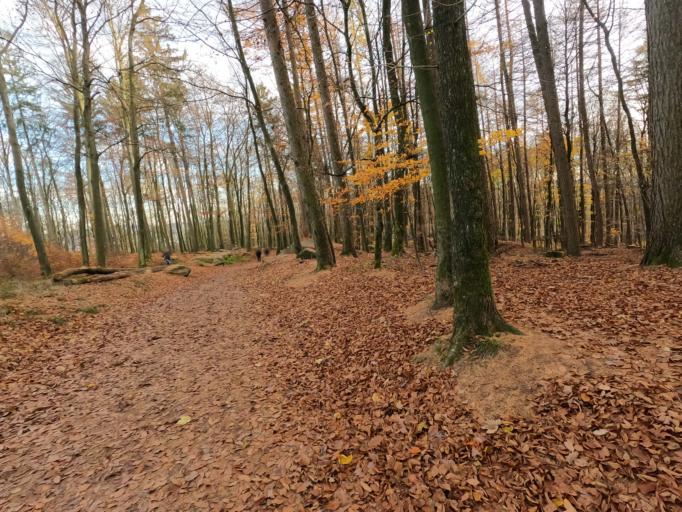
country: DE
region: Hesse
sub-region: Regierungsbezirk Darmstadt
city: Seeheim-Jugenheim
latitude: 49.7295
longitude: 8.6885
